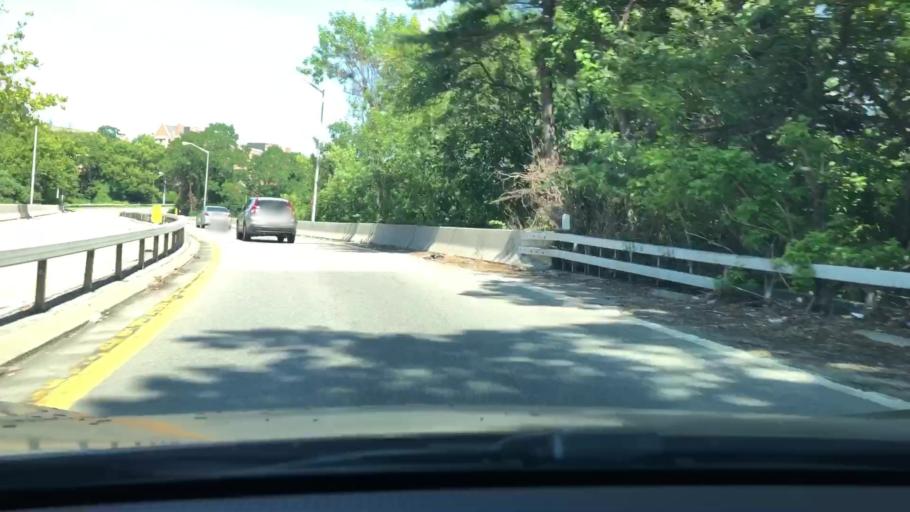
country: US
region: New York
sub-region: Westchester County
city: Mount Vernon
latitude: 40.9247
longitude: -73.8418
